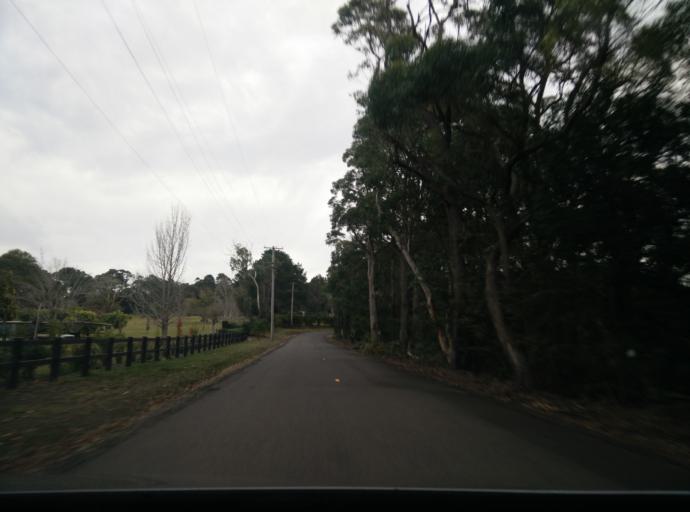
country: AU
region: New South Wales
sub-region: Gosford Shire
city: Narara
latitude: -33.3645
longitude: 151.3134
